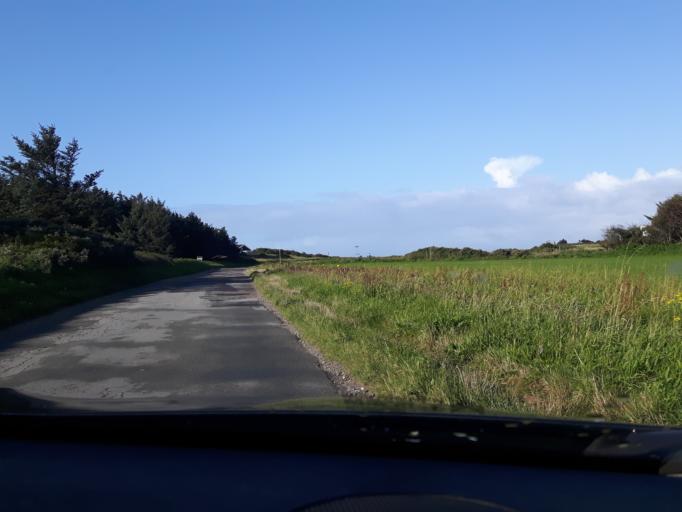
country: DK
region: North Denmark
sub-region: Hjorring Kommune
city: Hjorring
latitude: 57.4635
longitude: 9.7927
